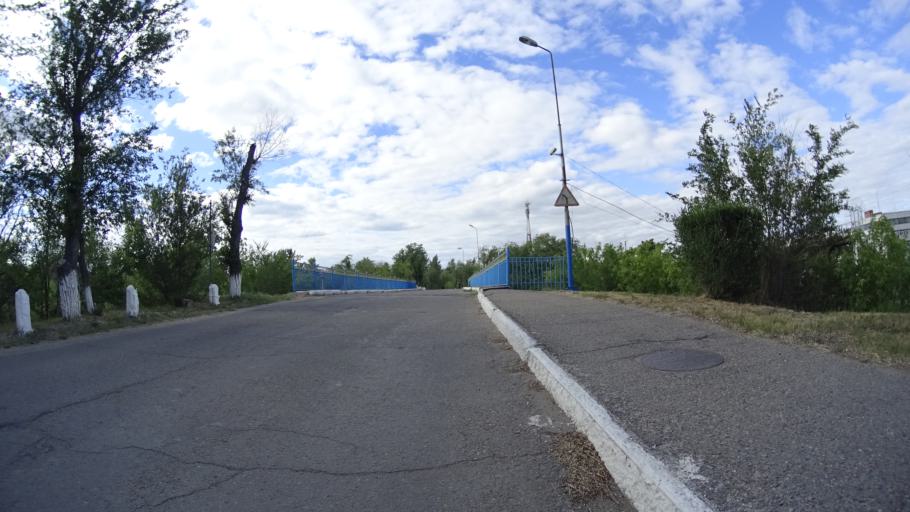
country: RU
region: Chelyabinsk
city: Troitsk
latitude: 54.0393
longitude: 61.6397
